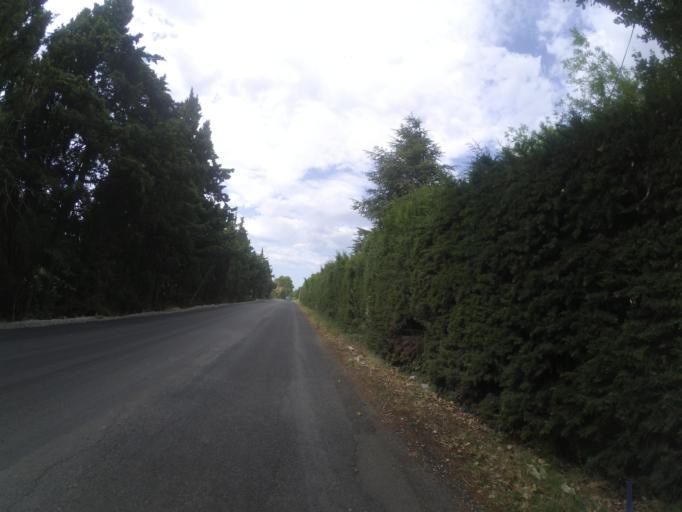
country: FR
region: Languedoc-Roussillon
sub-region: Departement des Pyrenees-Orientales
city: Toulouges
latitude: 42.6724
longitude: 2.8527
